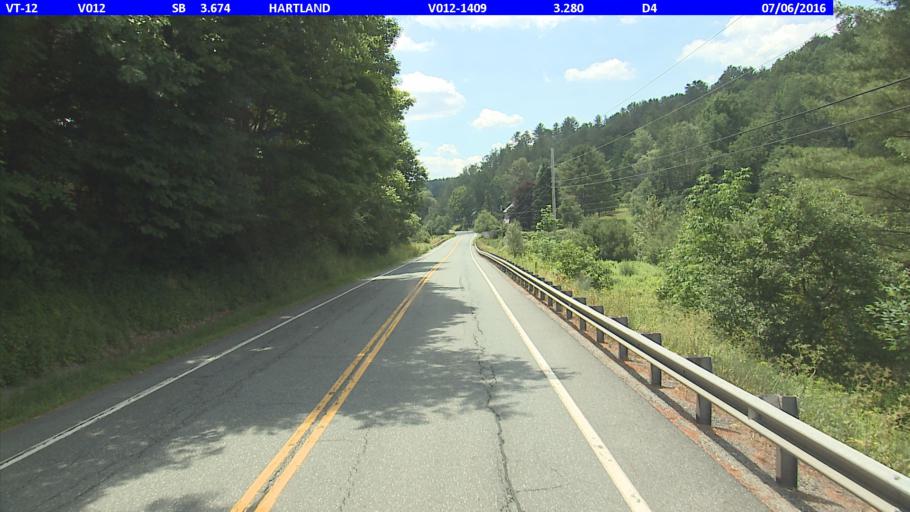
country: US
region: Vermont
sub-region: Windsor County
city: Woodstock
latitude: 43.5663
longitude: -72.4437
